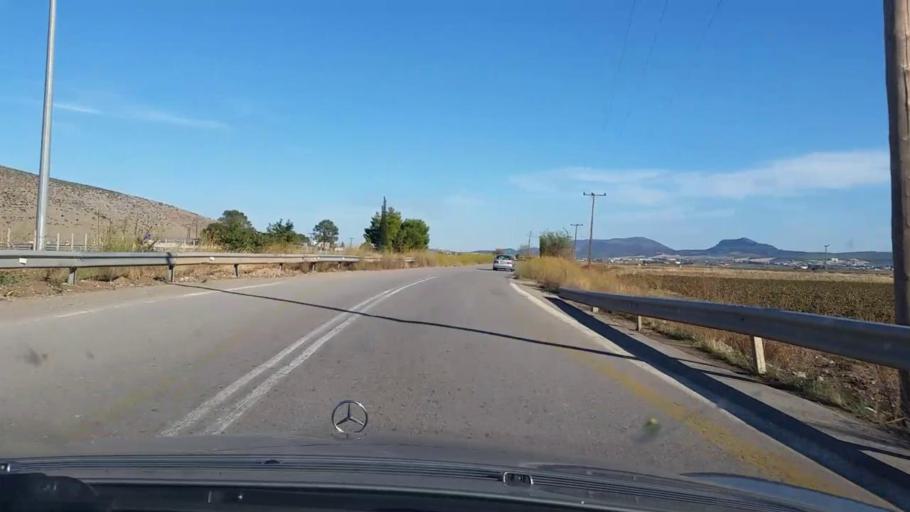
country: GR
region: Central Greece
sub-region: Nomos Voiotias
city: Thivai
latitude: 38.3702
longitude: 23.2875
